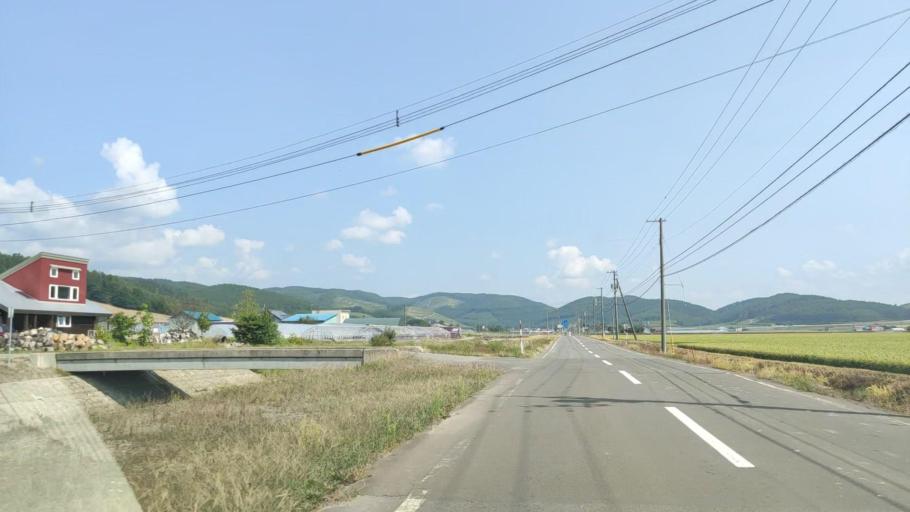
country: JP
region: Hokkaido
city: Shimo-furano
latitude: 43.3994
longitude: 142.3931
